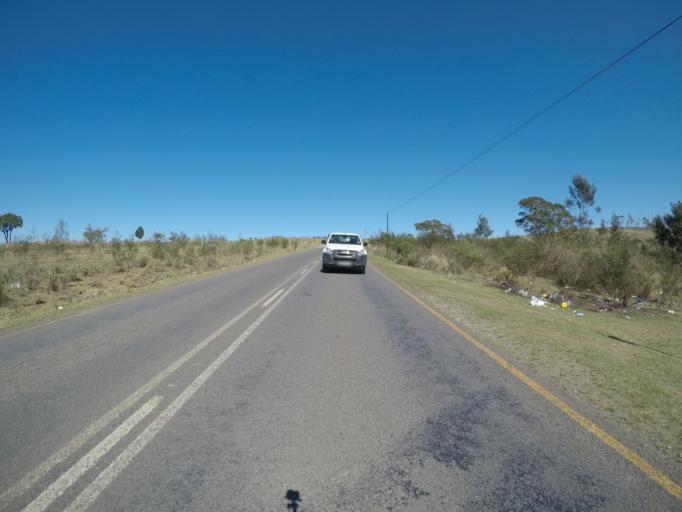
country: ZA
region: Eastern Cape
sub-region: OR Tambo District Municipality
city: Mthatha
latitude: -31.8067
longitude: 28.7591
